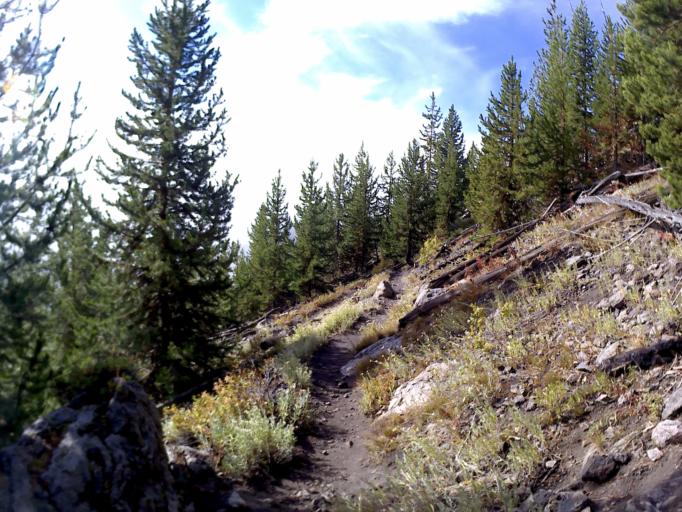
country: US
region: Montana
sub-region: Gallatin County
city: West Yellowstone
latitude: 44.4861
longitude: -110.8685
